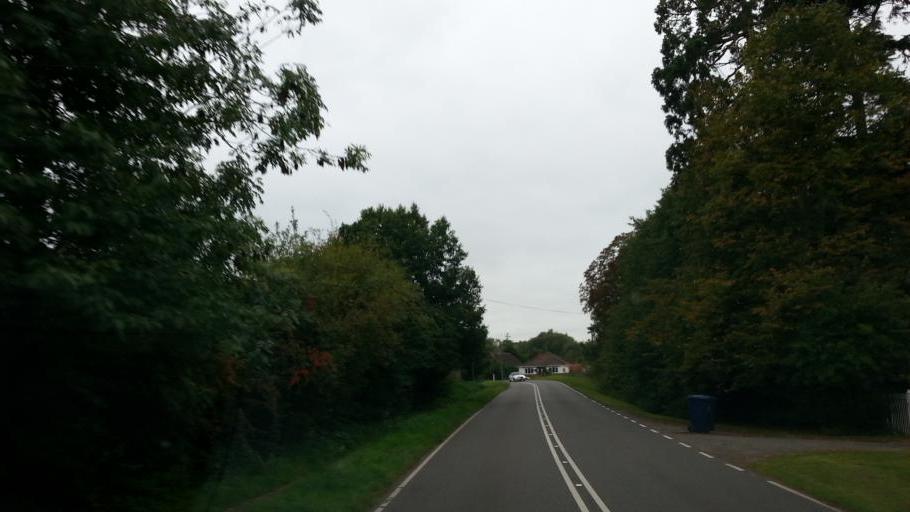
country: GB
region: England
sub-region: Cambridgeshire
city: Needingworth
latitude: 52.3343
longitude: -0.0256
